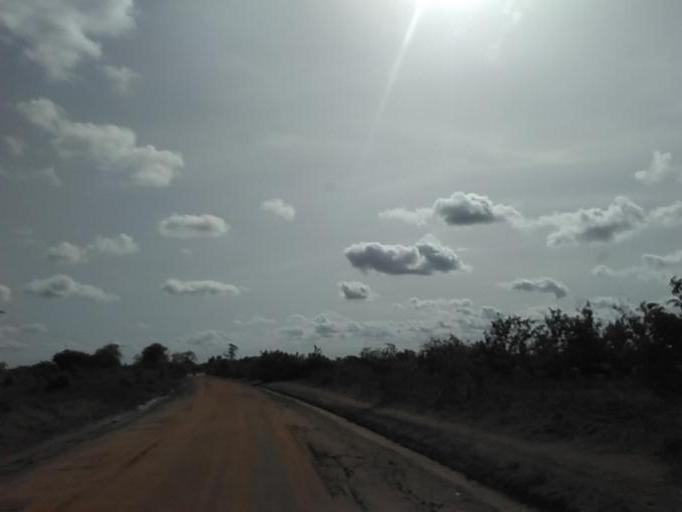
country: GH
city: Akropong
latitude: 6.0300
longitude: 0.3618
